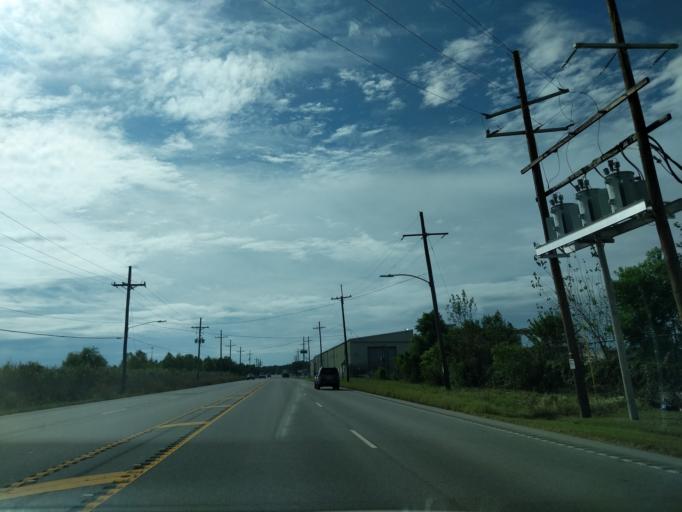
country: US
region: Louisiana
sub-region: Saint Tammany Parish
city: Eden Isle
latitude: 30.0770
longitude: -89.8498
